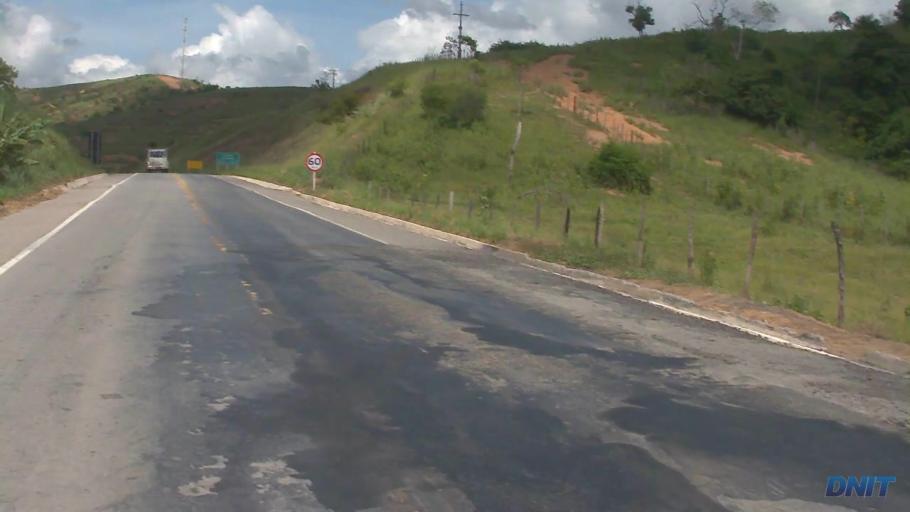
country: BR
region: Minas Gerais
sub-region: Governador Valadares
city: Governador Valadares
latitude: -19.0215
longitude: -42.1436
